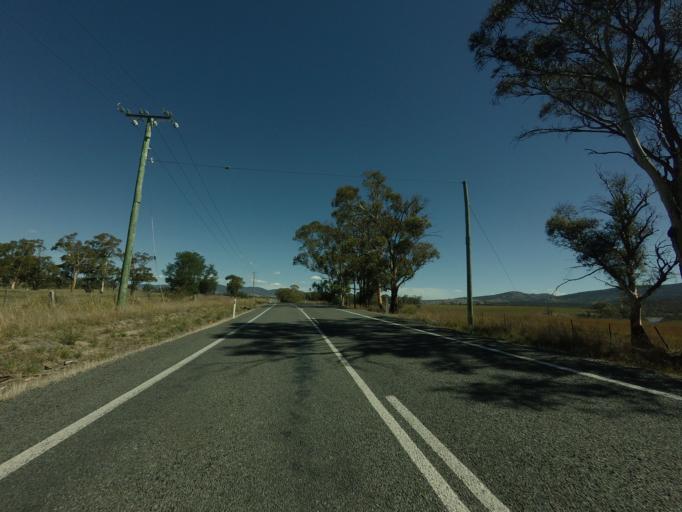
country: AU
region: Tasmania
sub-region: Northern Midlands
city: Evandale
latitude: -41.7581
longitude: 147.7536
